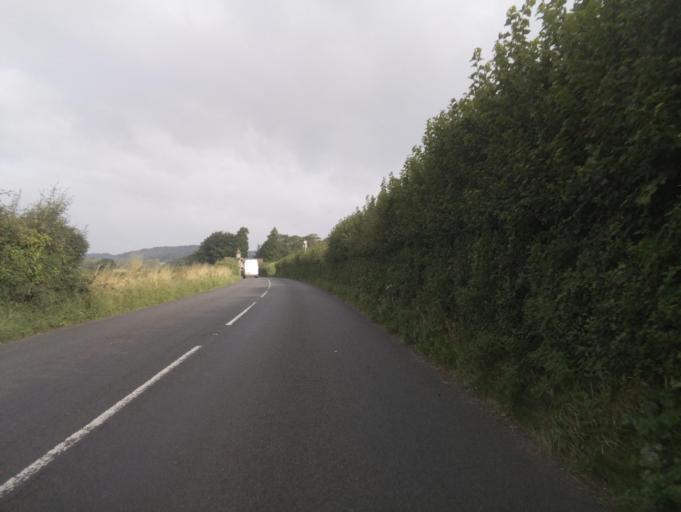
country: GB
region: England
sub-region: North Somerset
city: Long Ashton
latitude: 51.4278
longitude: -2.7019
